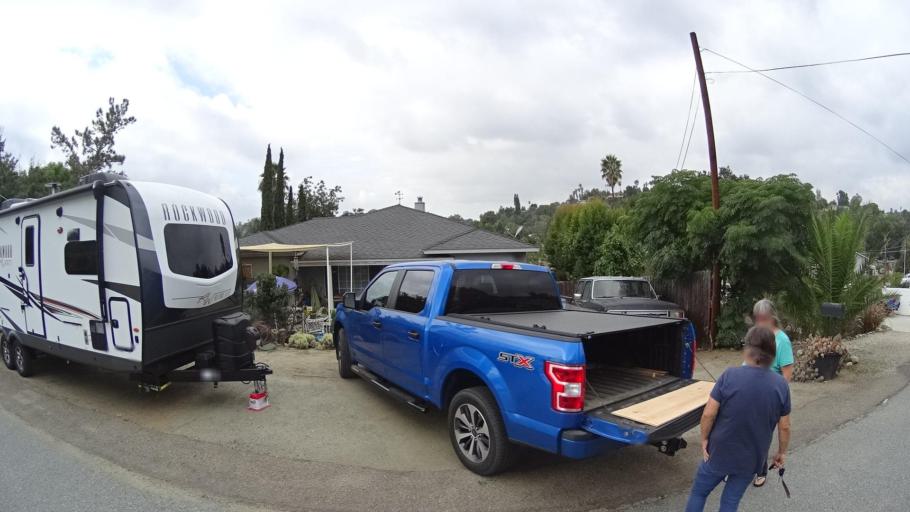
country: US
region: California
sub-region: San Diego County
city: Spring Valley
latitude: 32.7544
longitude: -116.9979
